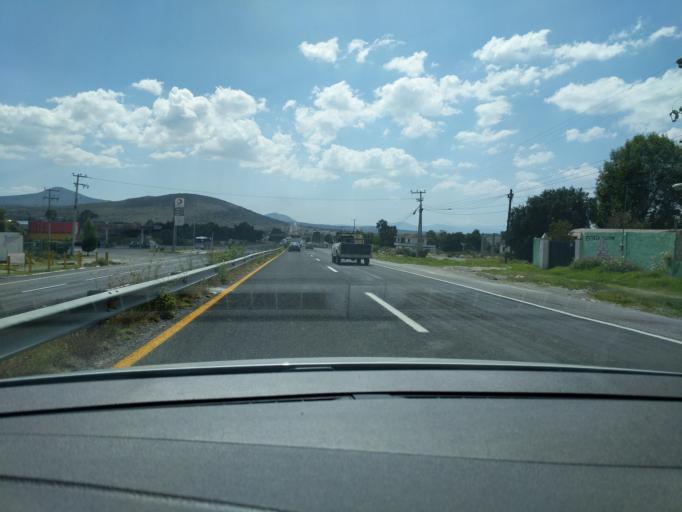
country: MX
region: Hidalgo
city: Zempoala
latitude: 19.9117
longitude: -98.6766
